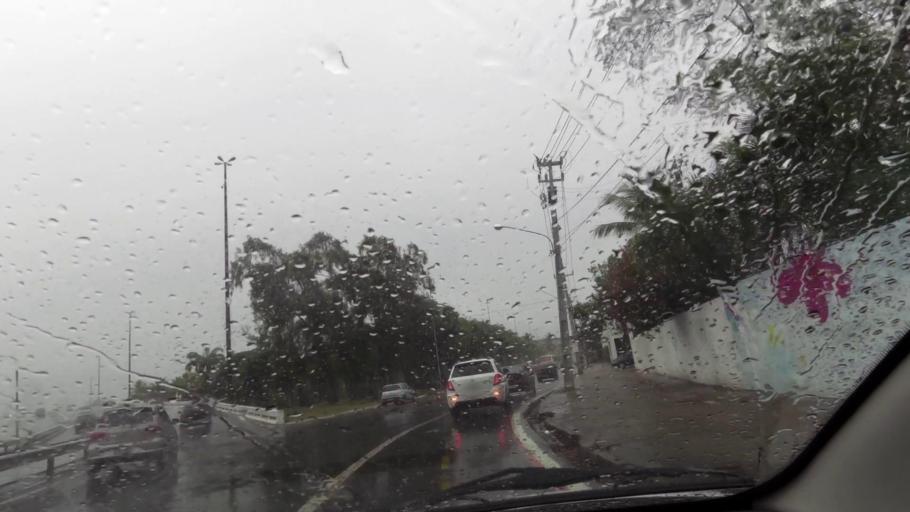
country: BR
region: Pernambuco
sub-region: Recife
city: Recife
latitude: -8.0793
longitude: -34.8919
